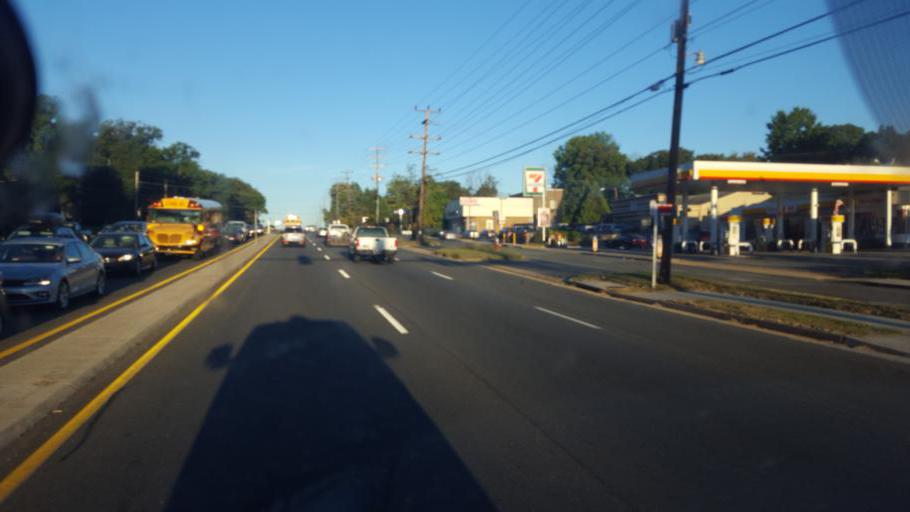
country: US
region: Virginia
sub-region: Fairfax County
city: Mantua
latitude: 38.8379
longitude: -77.2460
